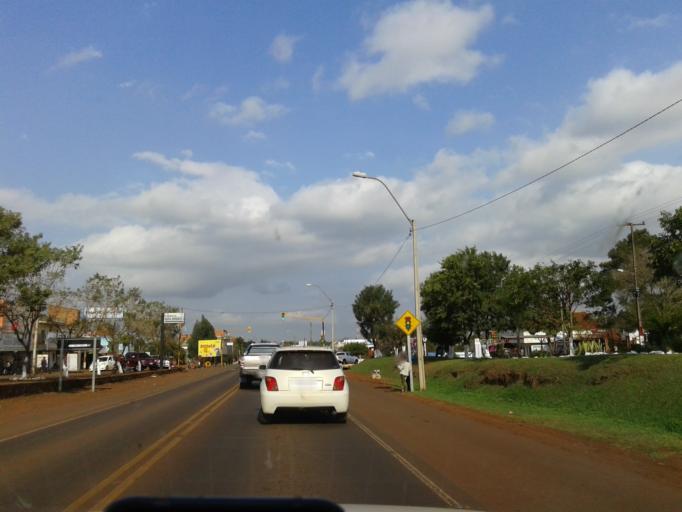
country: PY
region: Itapua
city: Arquitecto Tomas Romero Pereira
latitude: -26.5284
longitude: -55.2614
